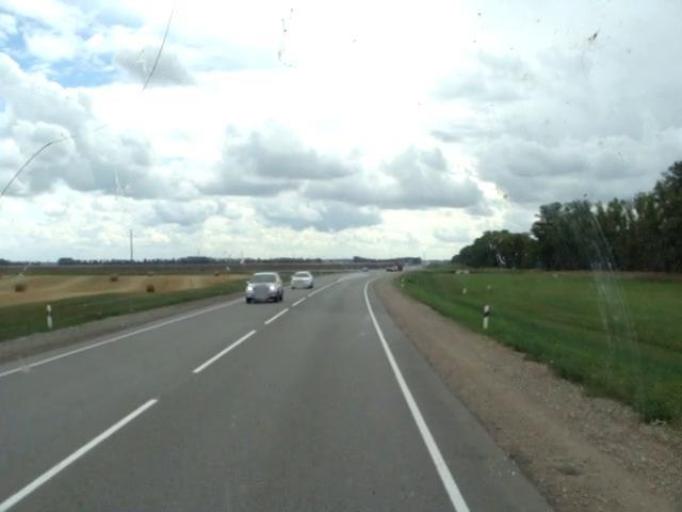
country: RU
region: Altai Krai
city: Shubenka
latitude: 52.6784
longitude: 85.0498
